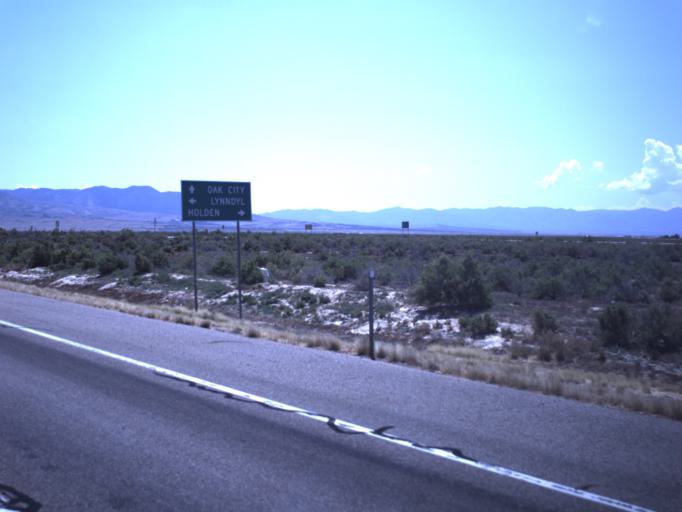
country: US
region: Utah
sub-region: Millard County
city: Delta
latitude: 39.3533
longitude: -112.4983
